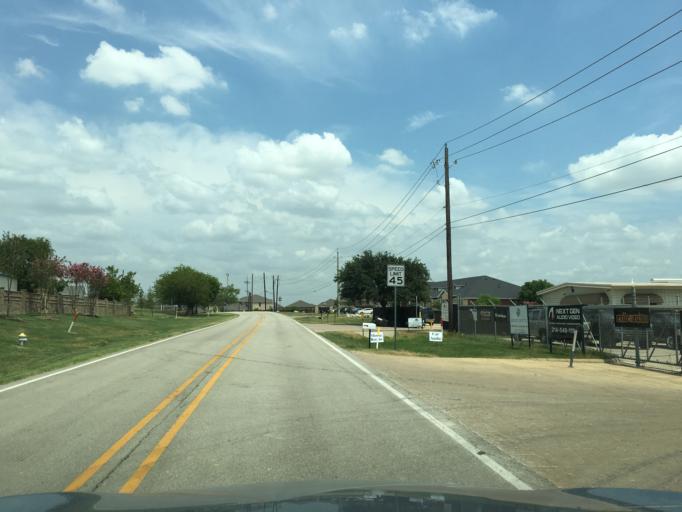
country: US
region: Texas
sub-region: Denton County
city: The Colony
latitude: 33.0404
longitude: -96.8620
